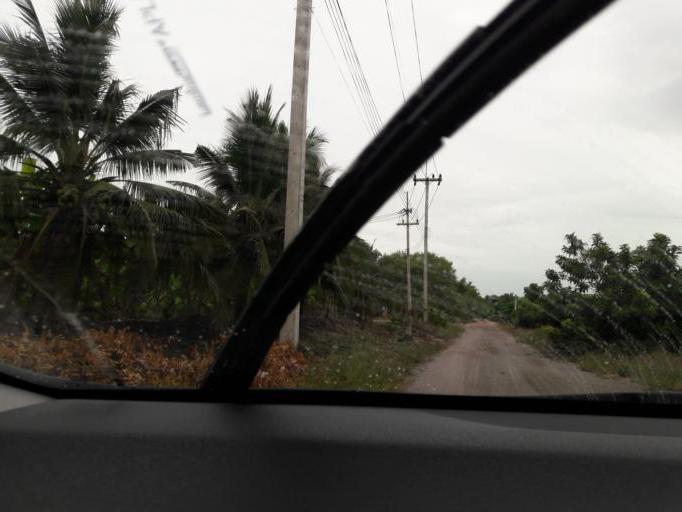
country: TH
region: Ratchaburi
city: Damnoen Saduak
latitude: 13.5706
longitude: 100.0167
